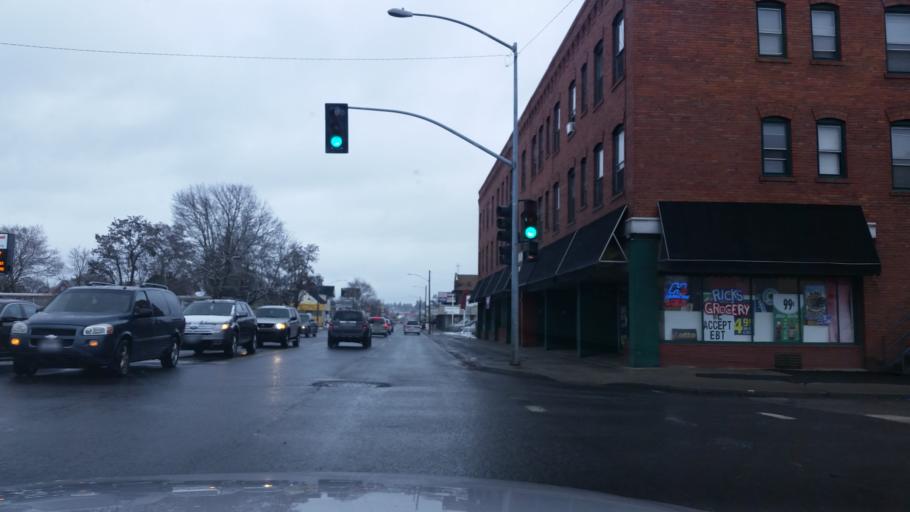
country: US
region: Washington
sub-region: Spokane County
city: Spokane
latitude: 47.6711
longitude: -117.4266
